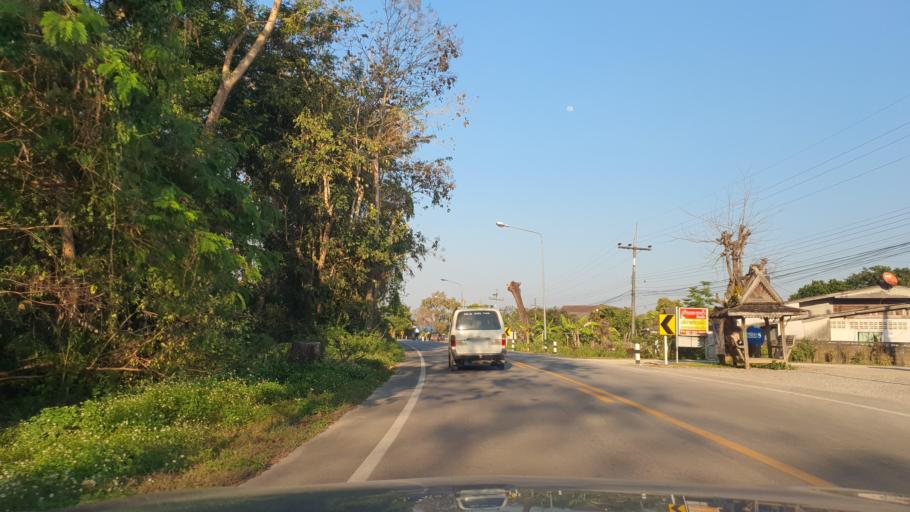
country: TH
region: Chiang Rai
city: Mae Lao
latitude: 19.8335
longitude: 99.6930
